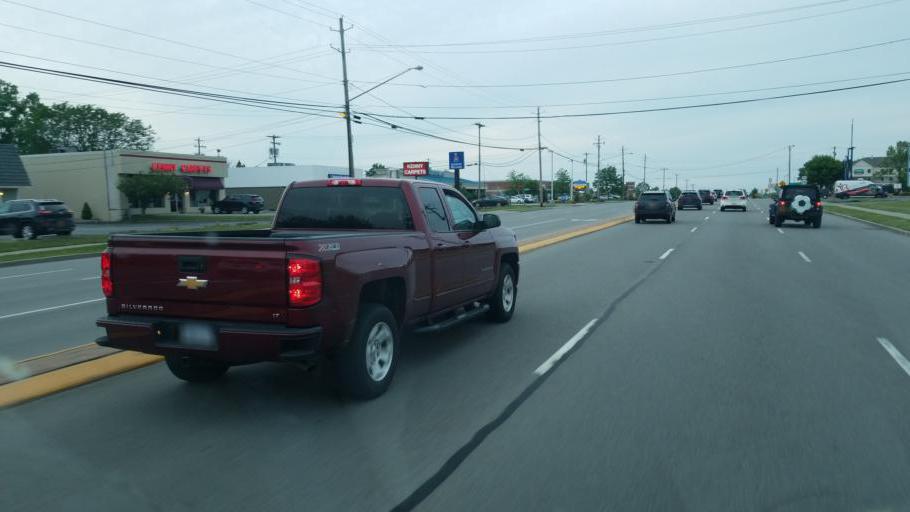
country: US
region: New York
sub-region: Erie County
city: Harris Hill
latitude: 42.9744
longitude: -78.6967
